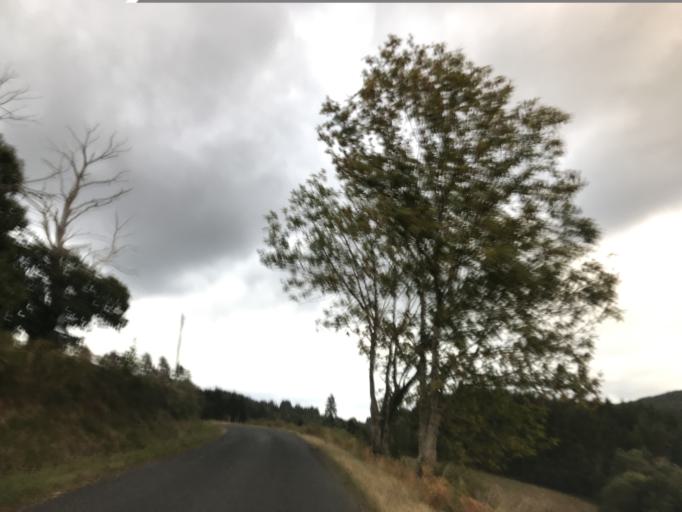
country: FR
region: Auvergne
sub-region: Departement du Puy-de-Dome
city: Celles-sur-Durolle
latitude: 45.8401
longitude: 3.6284
